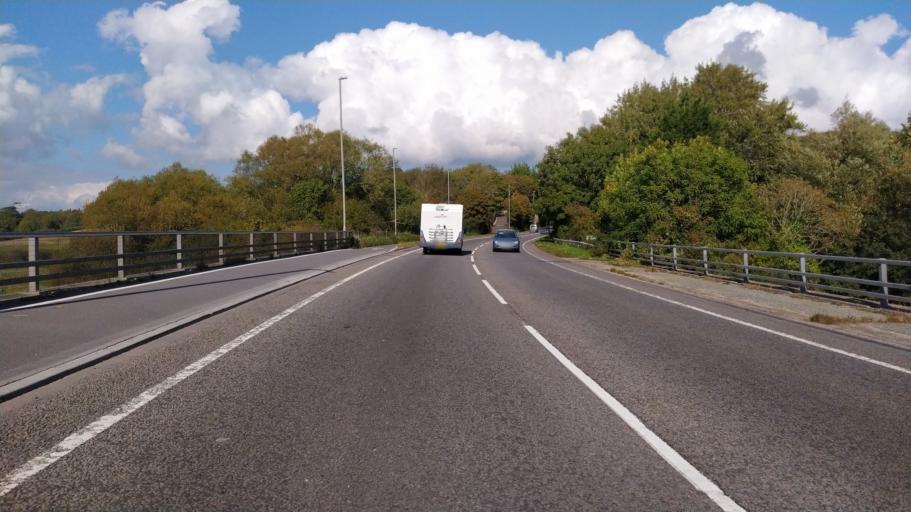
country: GB
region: England
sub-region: Dorset
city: Weymouth
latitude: 50.6285
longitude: -2.4724
